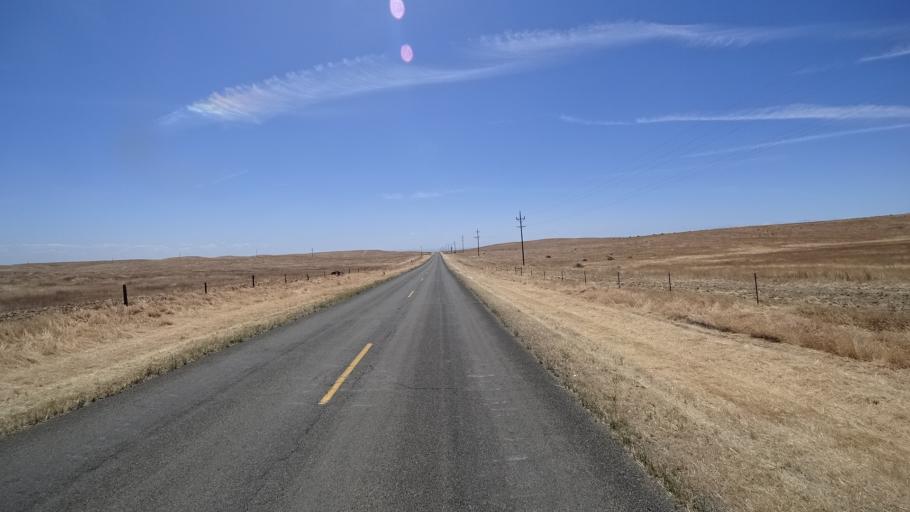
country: US
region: California
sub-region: Kings County
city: Kettleman City
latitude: 35.8805
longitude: -119.9151
